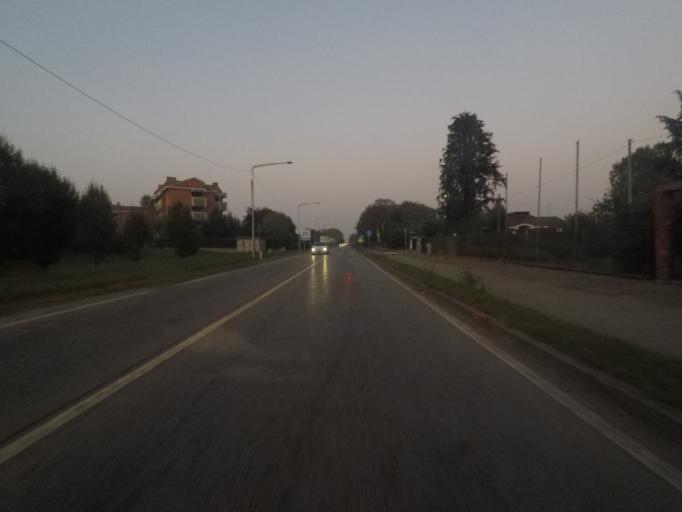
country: IT
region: Lombardy
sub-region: Provincia di Monza e Brianza
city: Brugherio
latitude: 45.5722
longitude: 9.3144
